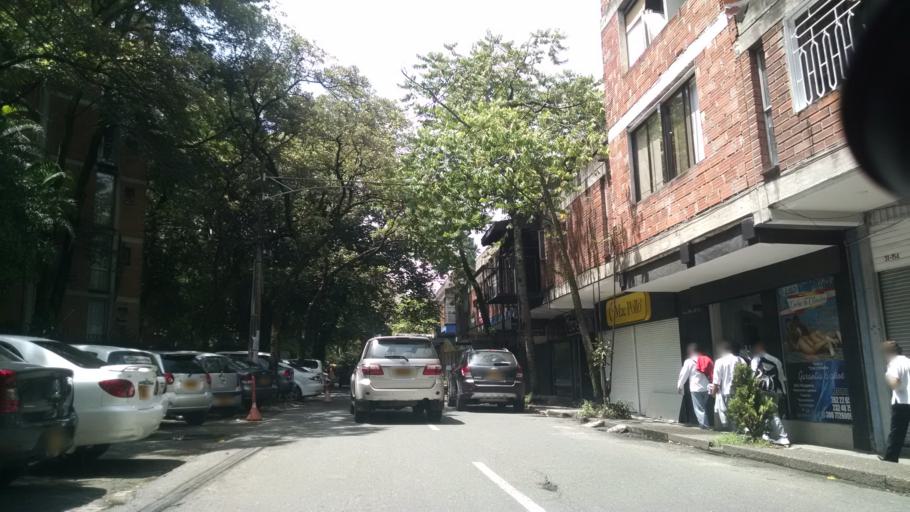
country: CO
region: Antioquia
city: Medellin
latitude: 6.2330
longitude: -75.5686
